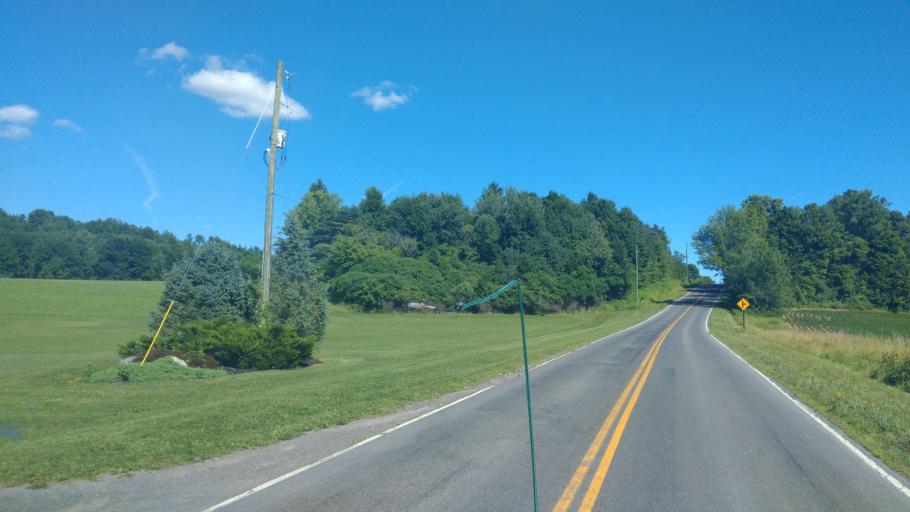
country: US
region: New York
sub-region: Wayne County
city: Clyde
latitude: 43.0260
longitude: -76.8291
